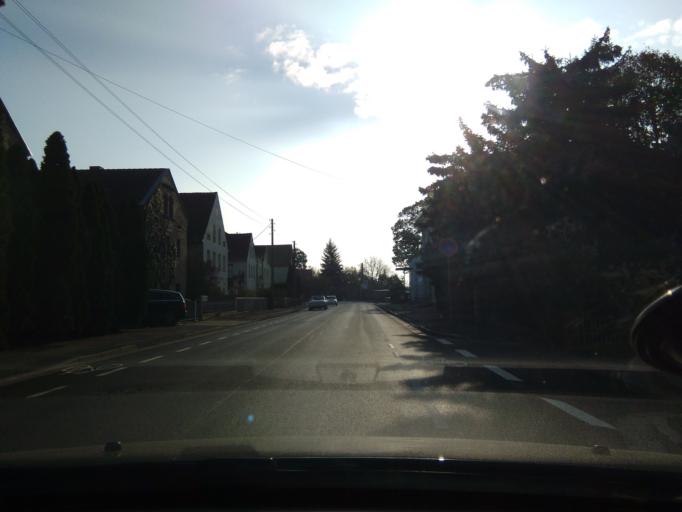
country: DE
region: Saxony
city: Coswig
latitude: 51.1302
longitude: 13.5450
